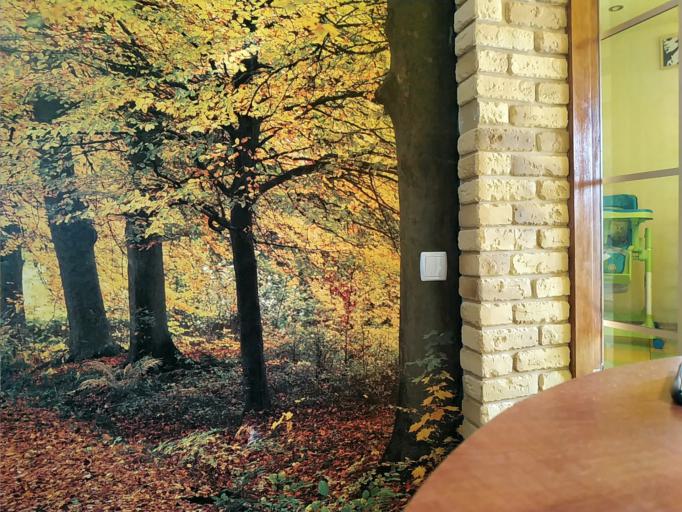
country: RU
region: Novgorod
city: Parfino
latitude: 57.7979
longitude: 31.6224
